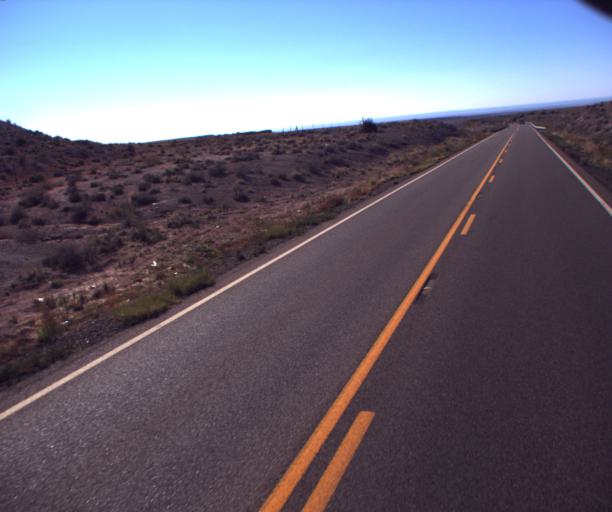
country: US
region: Arizona
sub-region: Navajo County
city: Dilkon
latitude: 35.1903
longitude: -110.4421
